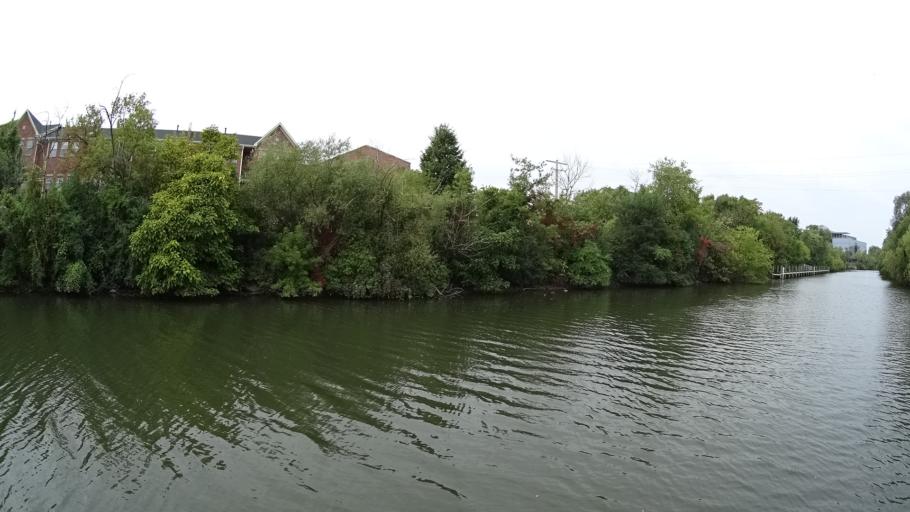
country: US
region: Illinois
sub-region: Cook County
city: Lincolnwood
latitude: 41.9402
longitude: -87.6935
